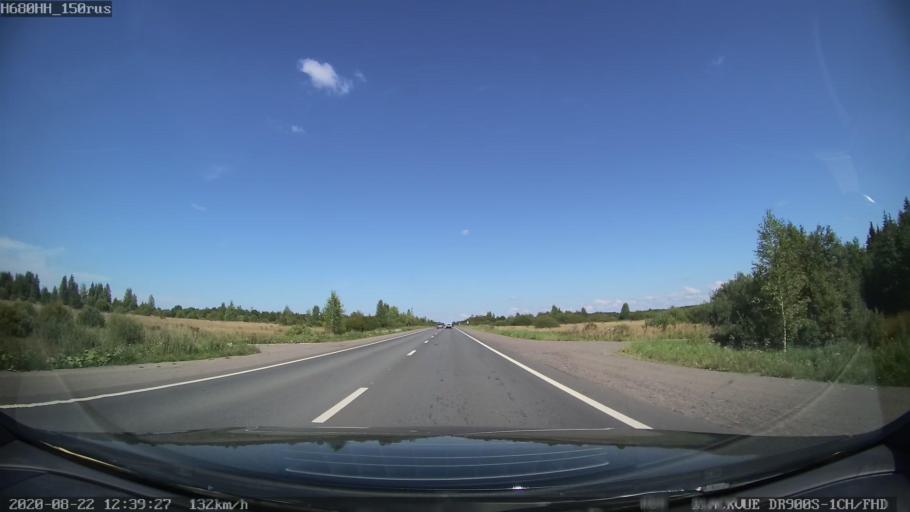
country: RU
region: Tverskaya
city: Rameshki
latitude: 57.3310
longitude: 36.0931
